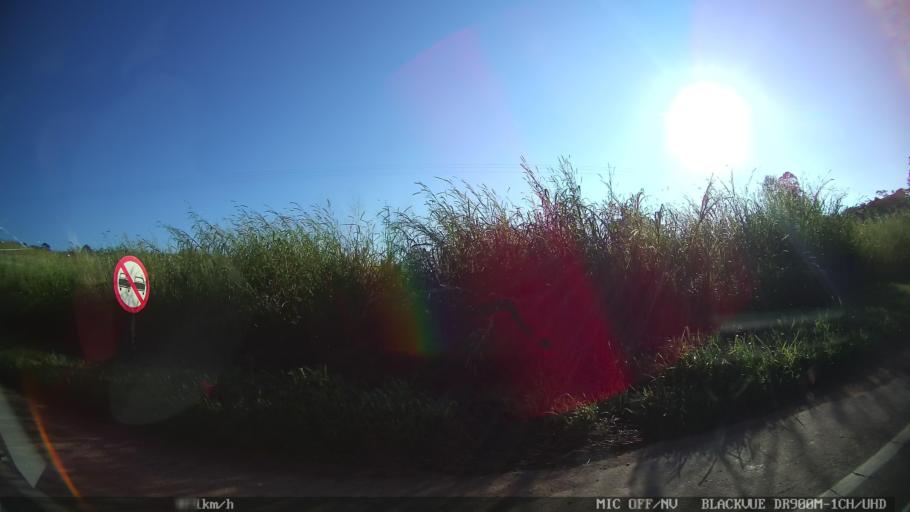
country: BR
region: Sao Paulo
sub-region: Vinhedo
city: Vinhedo
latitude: -23.0517
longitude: -47.0724
